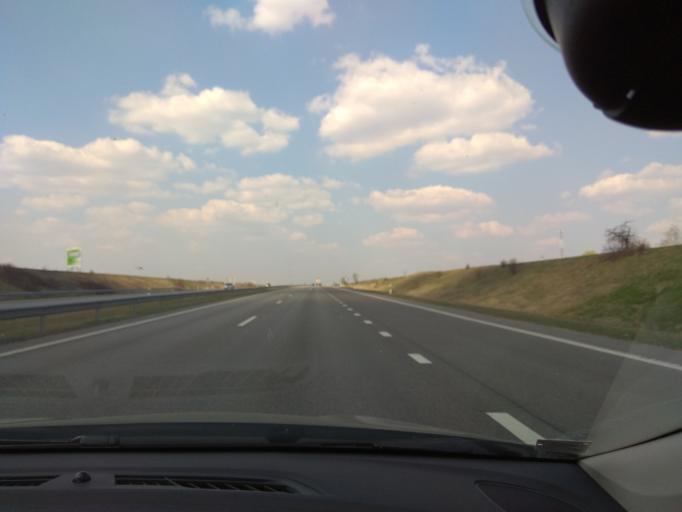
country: LT
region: Kauno apskritis
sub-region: Kaunas
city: Sargenai
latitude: 55.1106
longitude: 23.7739
